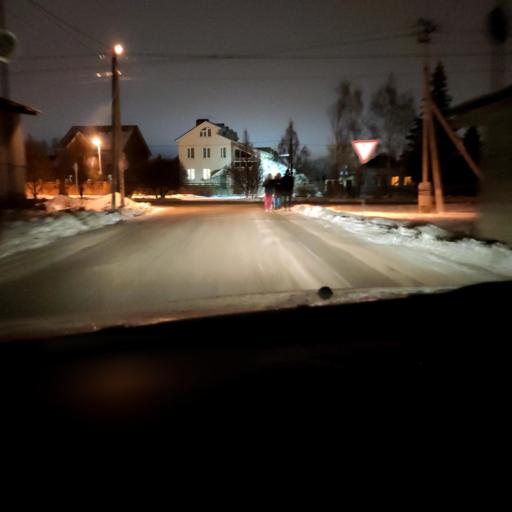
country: RU
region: Samara
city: Smyshlyayevka
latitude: 53.2533
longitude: 50.3956
